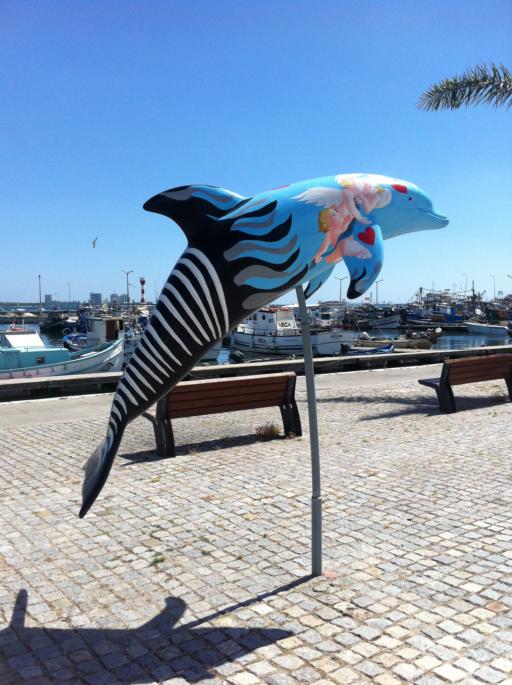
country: PT
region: Setubal
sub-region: Setubal
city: Setubal
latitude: 38.5202
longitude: -8.8997
